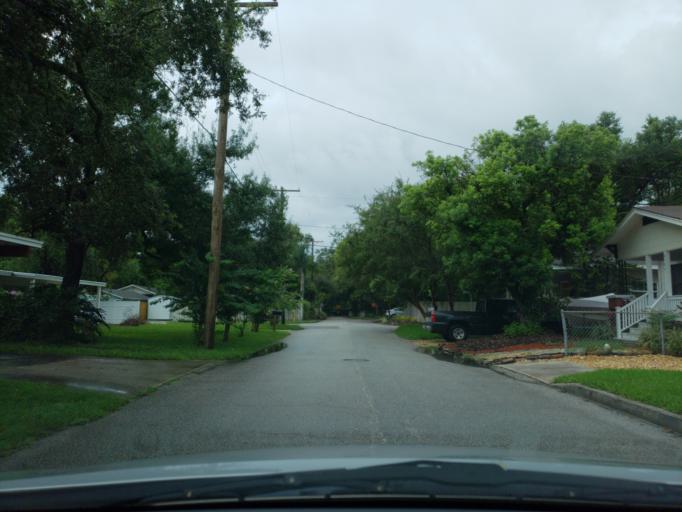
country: US
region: Florida
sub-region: Hillsborough County
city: Egypt Lake-Leto
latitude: 28.0084
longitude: -82.4616
